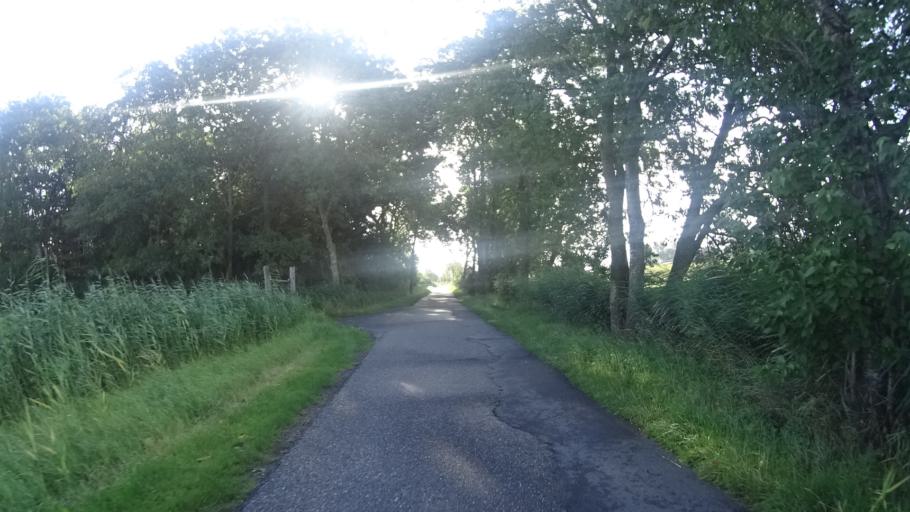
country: DE
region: Lower Saxony
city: Nordenham
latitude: 53.4966
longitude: 8.4325
